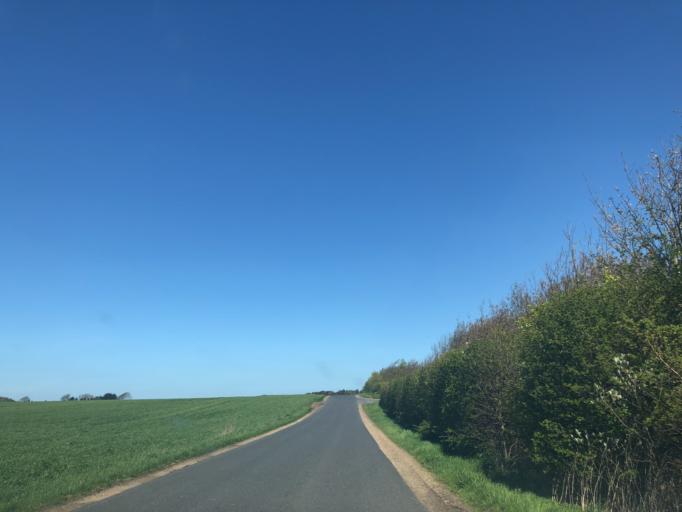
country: DK
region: Central Jutland
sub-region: Holstebro Kommune
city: Vinderup
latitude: 56.5246
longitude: 8.7773
